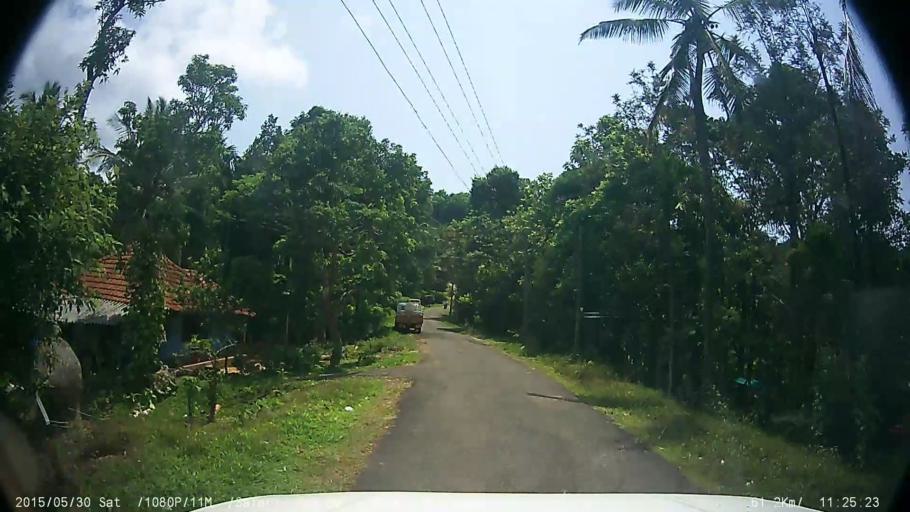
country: IN
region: Kerala
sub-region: Wayanad
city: Panamaram
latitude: 11.8101
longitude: 76.0318
